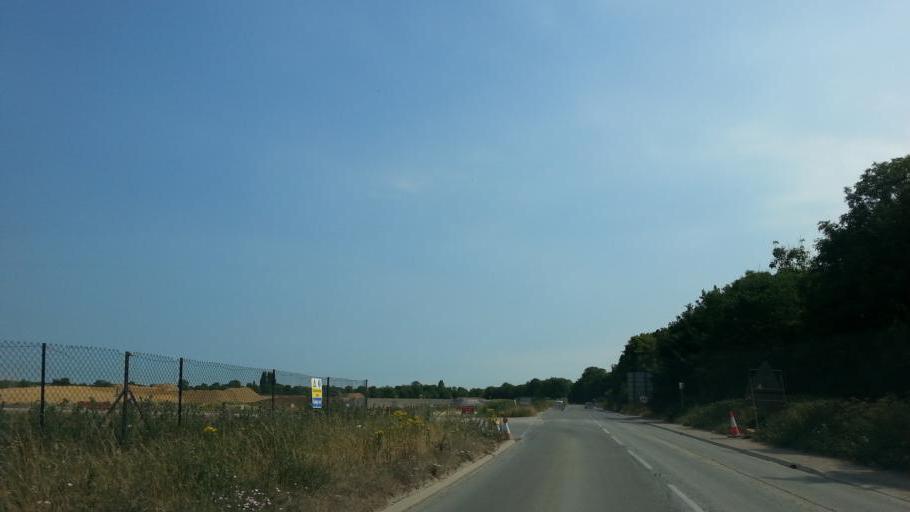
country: GB
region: England
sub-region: Cambridgeshire
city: Buckden
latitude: 52.3067
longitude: -0.2357
